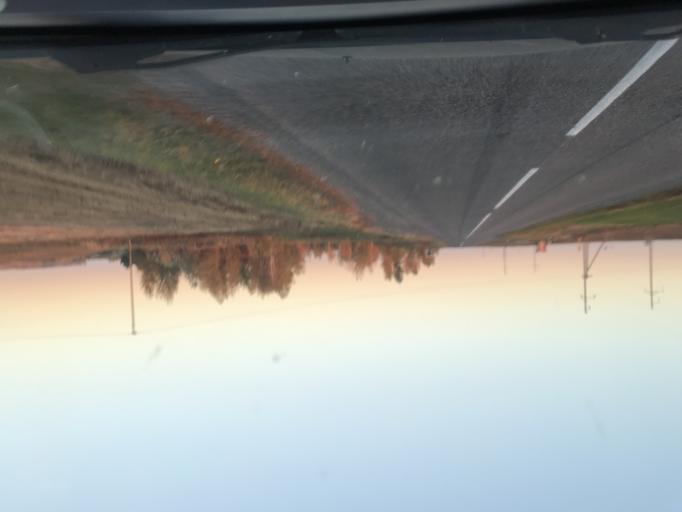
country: BY
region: Gomel
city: Loyew
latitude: 52.1119
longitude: 30.5728
